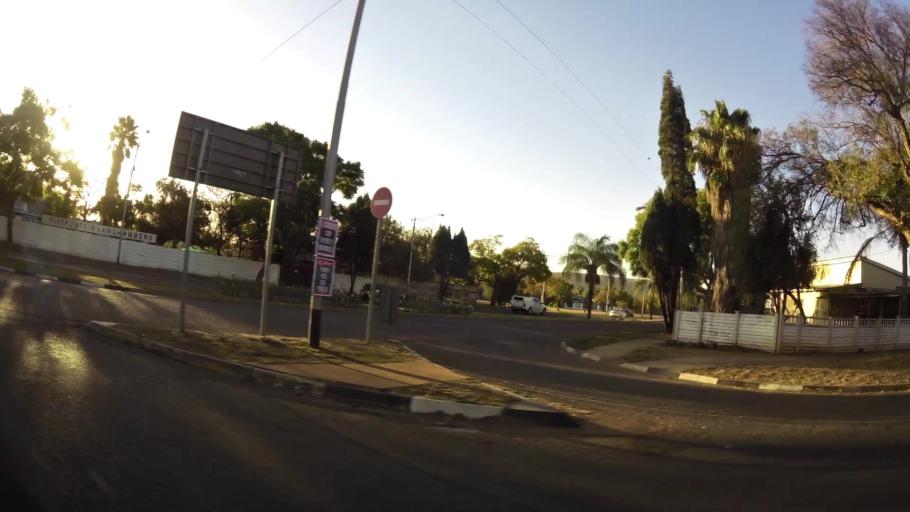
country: ZA
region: Gauteng
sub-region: City of Tshwane Metropolitan Municipality
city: Pretoria
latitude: -25.7151
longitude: 28.2220
